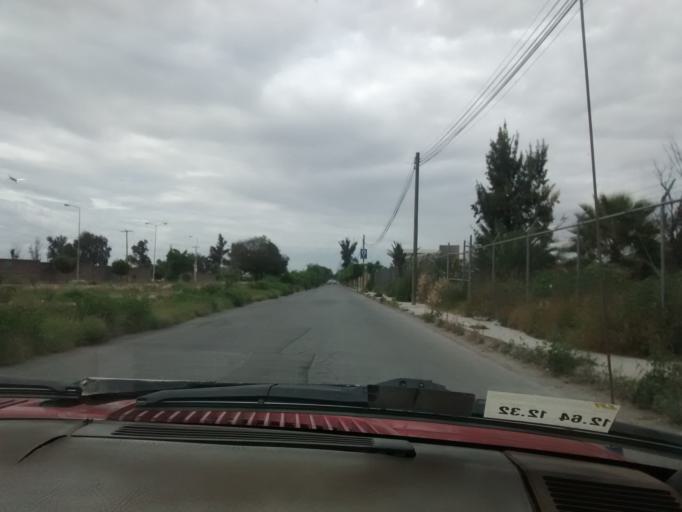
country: MX
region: Puebla
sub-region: Santiago Miahuatlan
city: San Isidro Vista Hermosa
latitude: 18.4834
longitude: -97.4138
